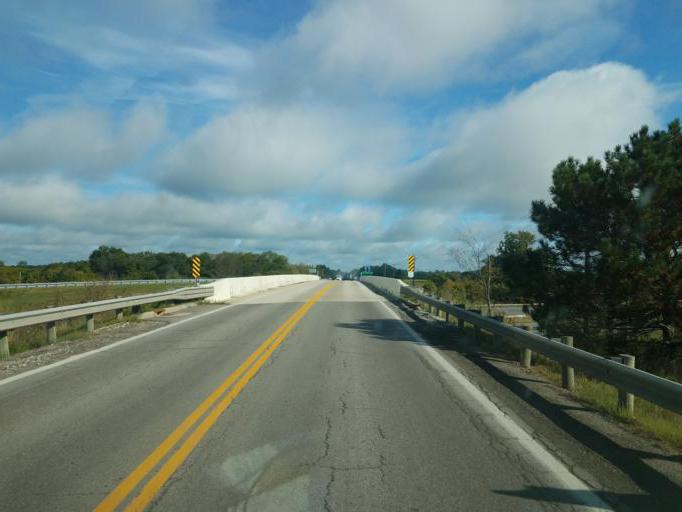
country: US
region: Ohio
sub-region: Wayne County
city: West Salem
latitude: 40.9347
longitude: -82.1092
